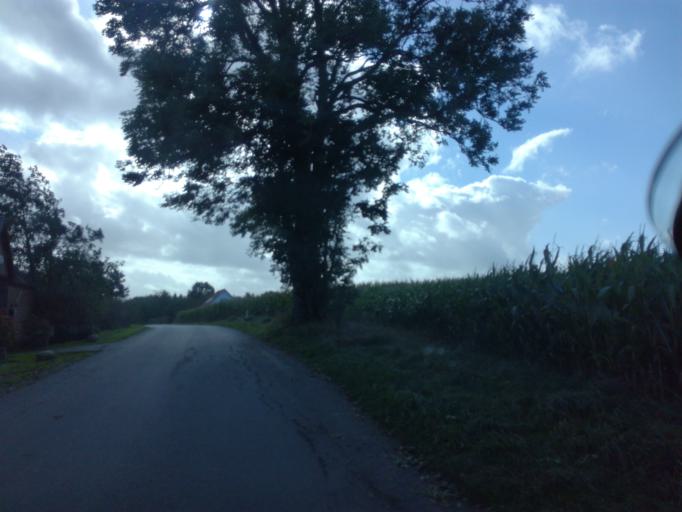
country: DK
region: South Denmark
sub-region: Vejle Kommune
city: Brejning
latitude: 55.6335
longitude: 9.7166
